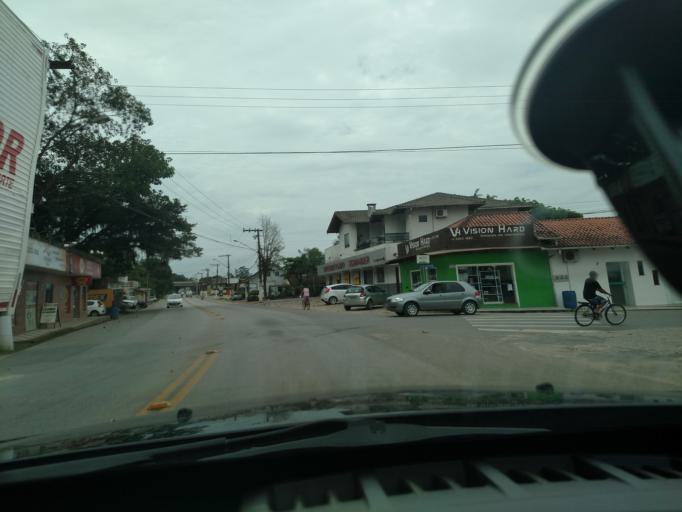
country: BR
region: Santa Catarina
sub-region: Gaspar
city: Gaspar
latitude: -26.8987
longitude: -48.8261
